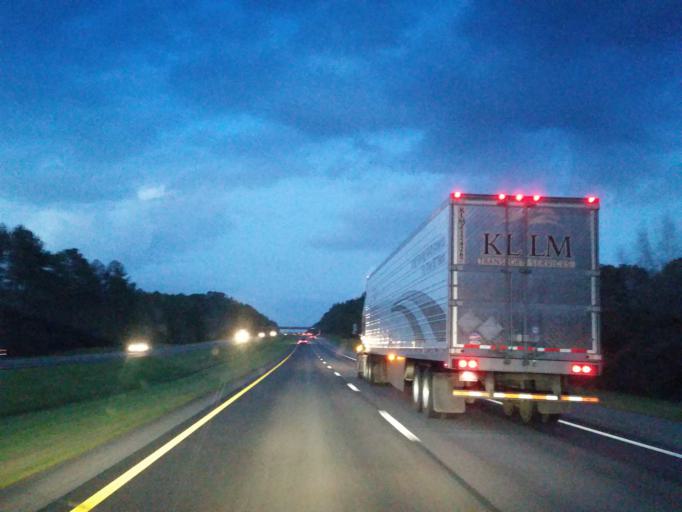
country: US
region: Alabama
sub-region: Sumter County
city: Livingston
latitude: 32.5899
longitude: -88.2274
